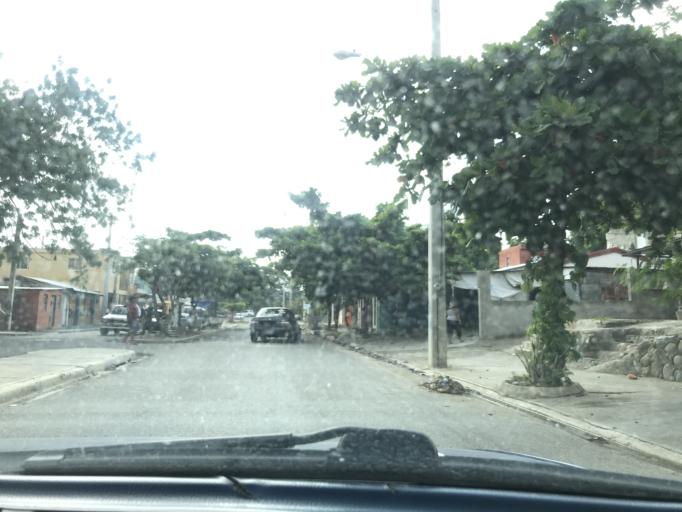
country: DO
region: Santiago
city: Santiago de los Caballeros
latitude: 19.4491
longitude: -70.7316
